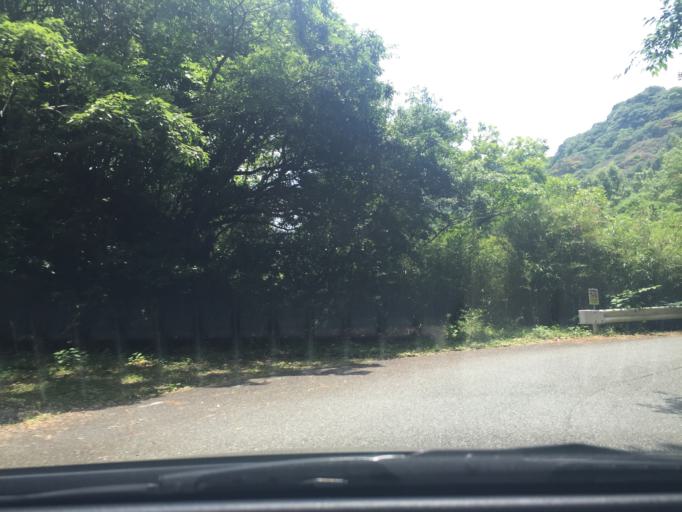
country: JP
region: Shizuoka
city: Shimoda
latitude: 34.7116
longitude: 138.8105
